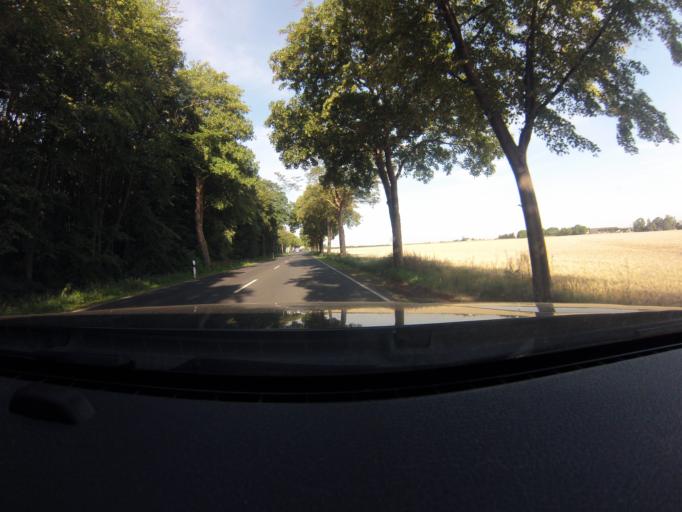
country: DE
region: North Rhine-Westphalia
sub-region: Regierungsbezirk Koln
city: Rheinbach
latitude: 50.6780
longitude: 6.9475
